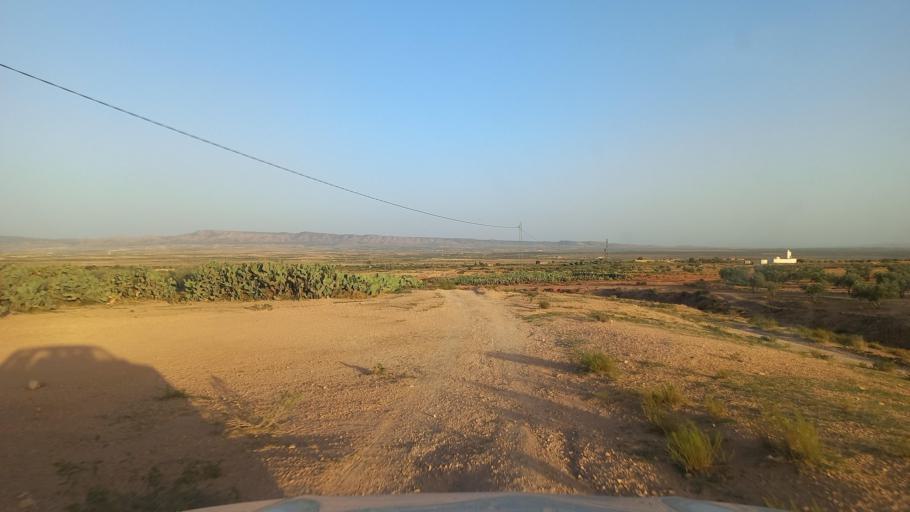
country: TN
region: Al Qasrayn
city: Sbiba
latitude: 35.3729
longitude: 9.0060
